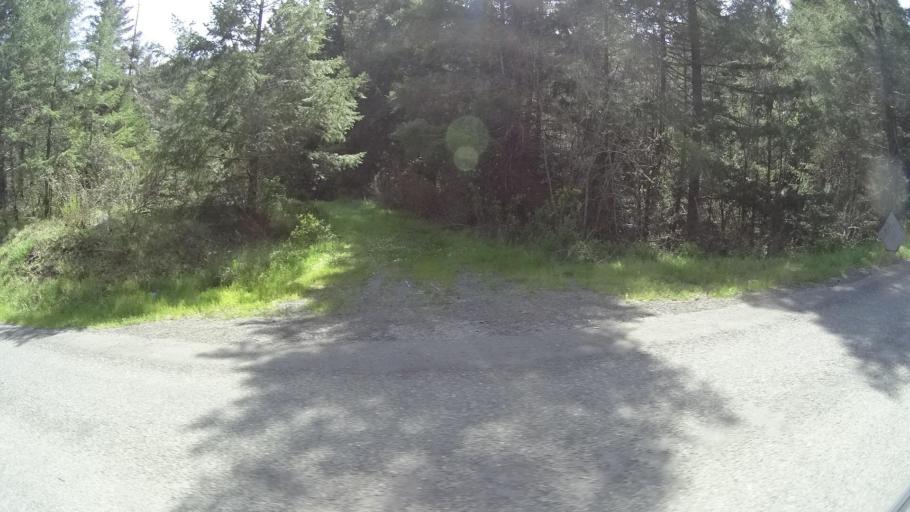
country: US
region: California
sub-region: Humboldt County
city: Redway
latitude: 40.4375
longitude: -123.7783
